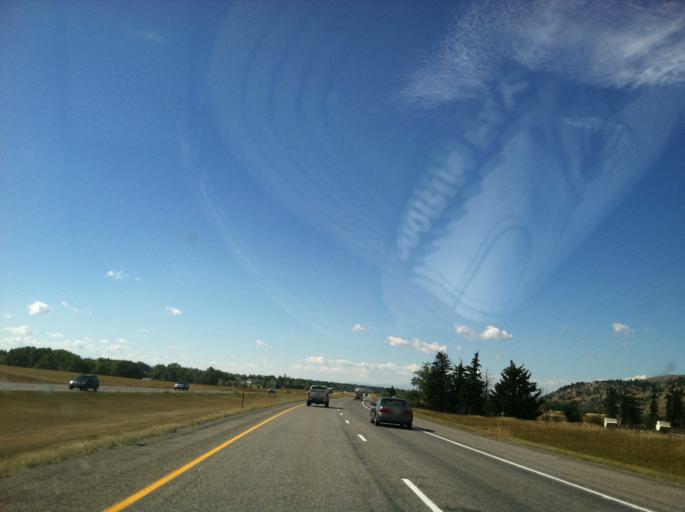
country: US
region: Montana
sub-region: Gallatin County
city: Bozeman
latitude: 45.6646
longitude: -110.9733
